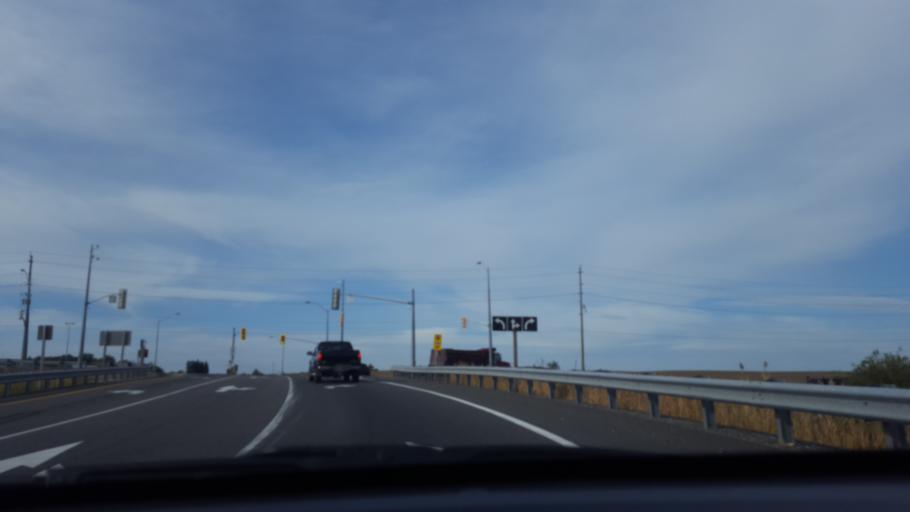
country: CA
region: Ontario
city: Vaughan
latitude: 43.9202
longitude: -79.5638
